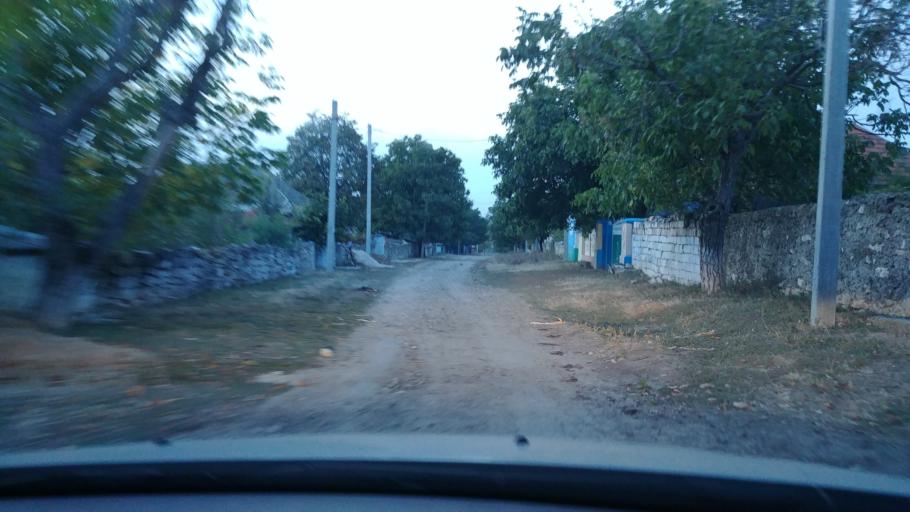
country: MD
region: Rezina
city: Saharna
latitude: 47.6772
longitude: 28.9600
